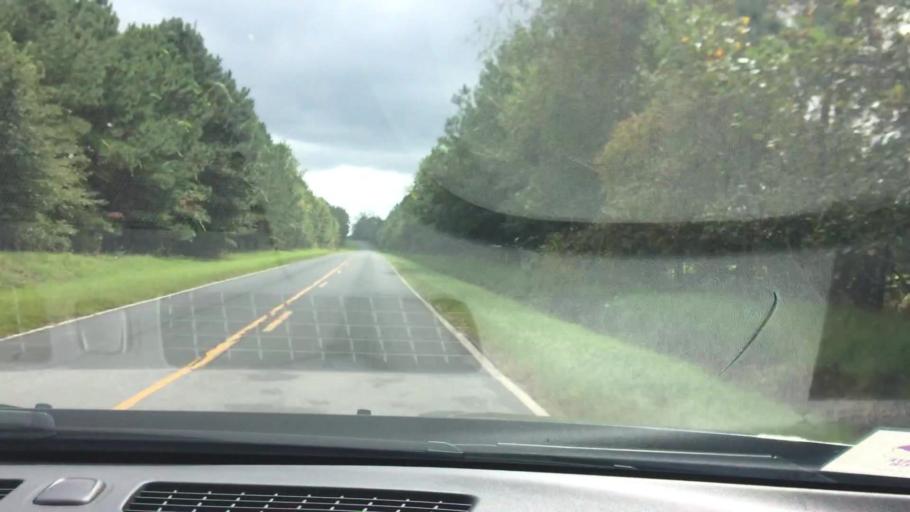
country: US
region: North Carolina
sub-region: Greene County
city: Maury
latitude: 35.5311
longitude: -77.5451
